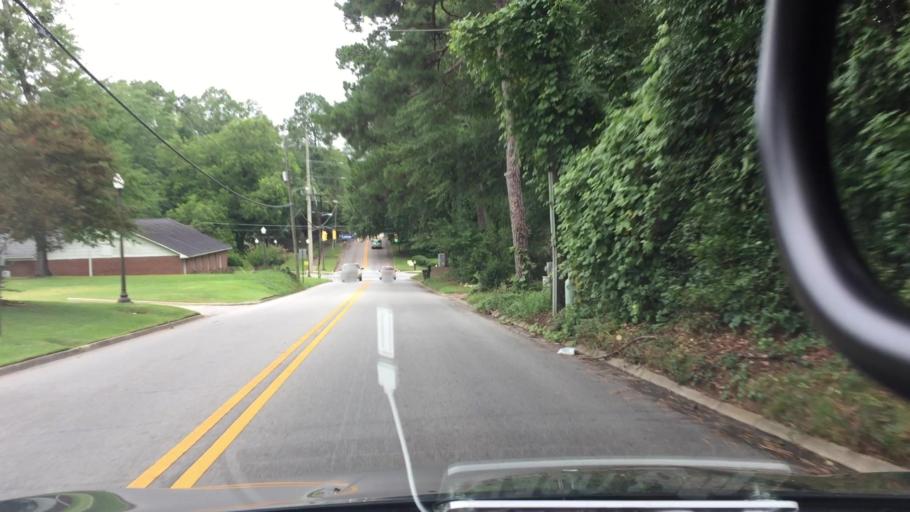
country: US
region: Alabama
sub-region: Lee County
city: Auburn
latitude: 32.6142
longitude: -85.4805
